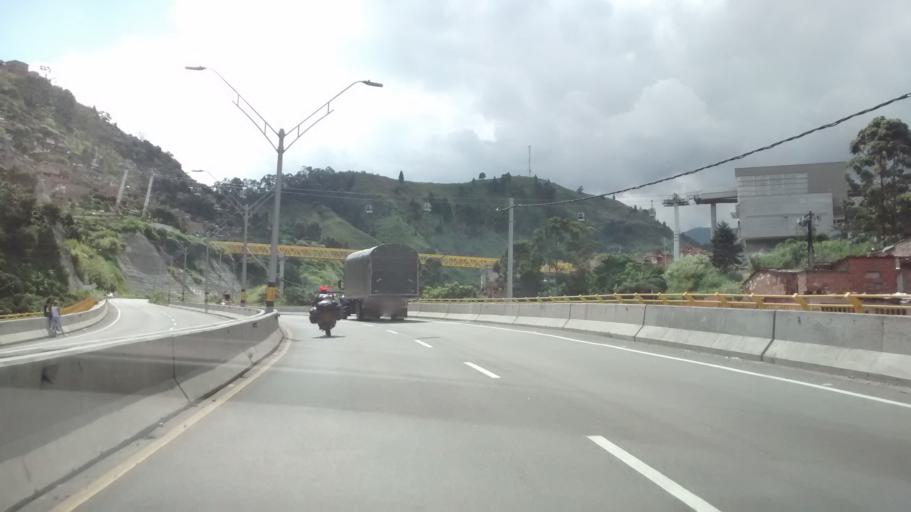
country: CO
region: Antioquia
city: Medellin
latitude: 6.2755
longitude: -75.6118
